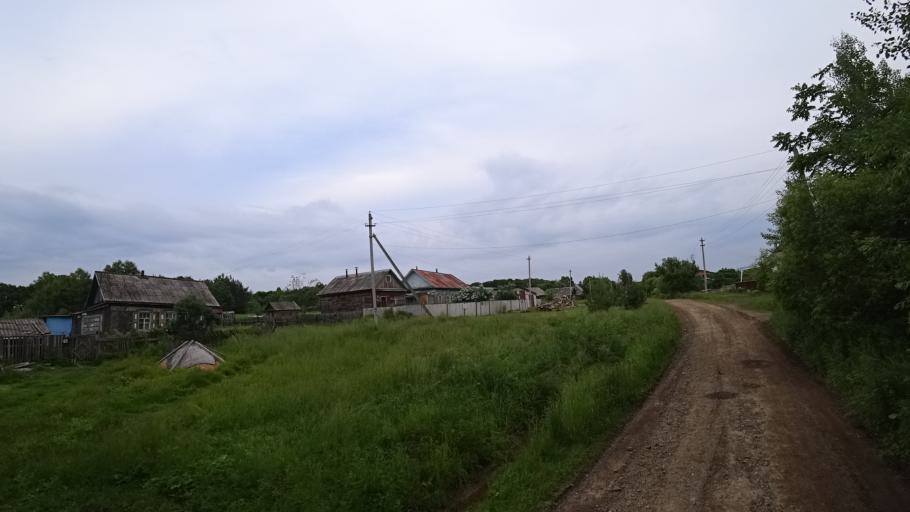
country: RU
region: Primorskiy
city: Novosysoyevka
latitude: 44.2467
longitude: 133.3786
